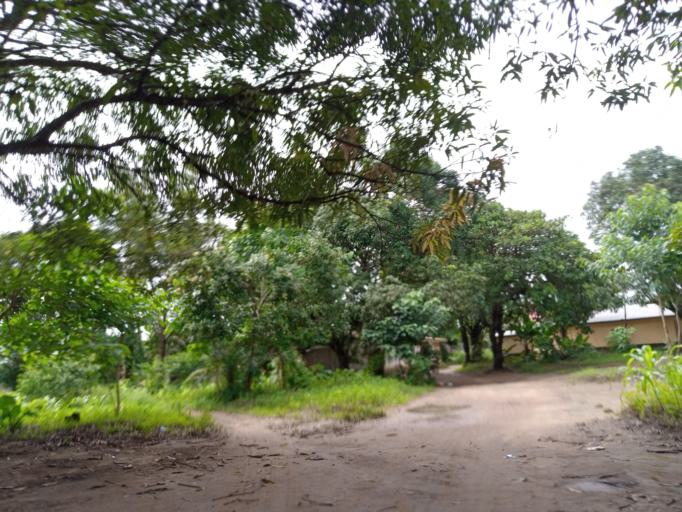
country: SL
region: Northern Province
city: Sawkta
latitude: 8.6253
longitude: -13.2031
